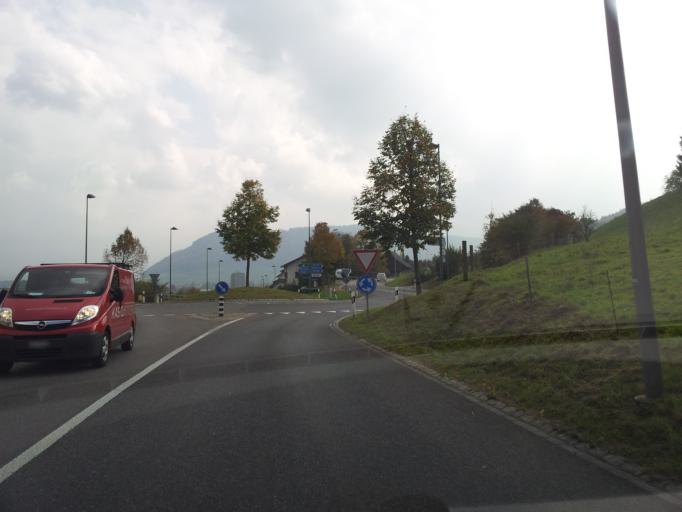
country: CH
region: Bern
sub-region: Bern-Mittelland District
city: Kehrsatz
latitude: 46.9015
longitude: 7.4850
